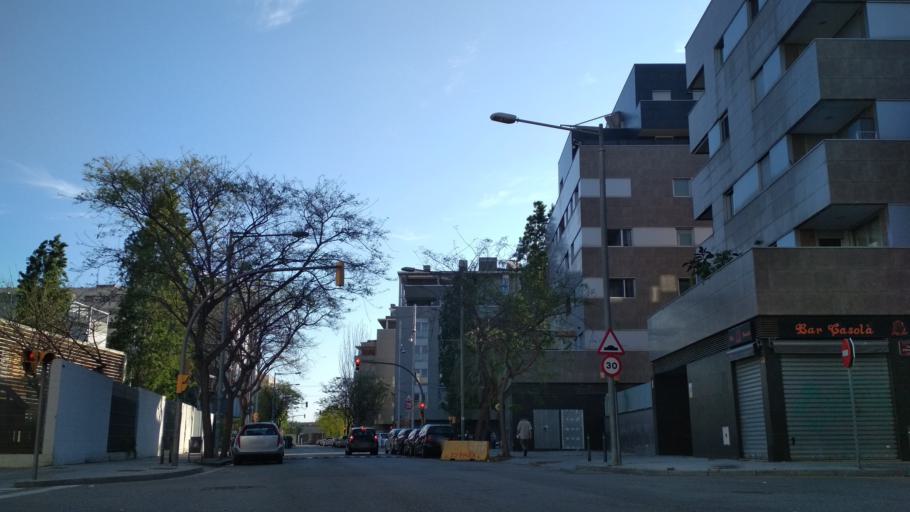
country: ES
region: Catalonia
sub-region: Provincia de Barcelona
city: Sant Adria de Besos
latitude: 41.4170
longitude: 2.2213
